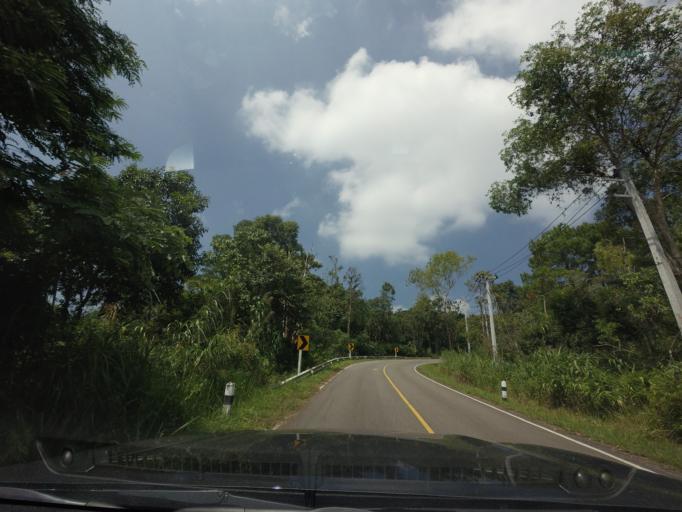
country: TH
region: Loei
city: Na Haeo
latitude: 17.4798
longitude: 100.9155
